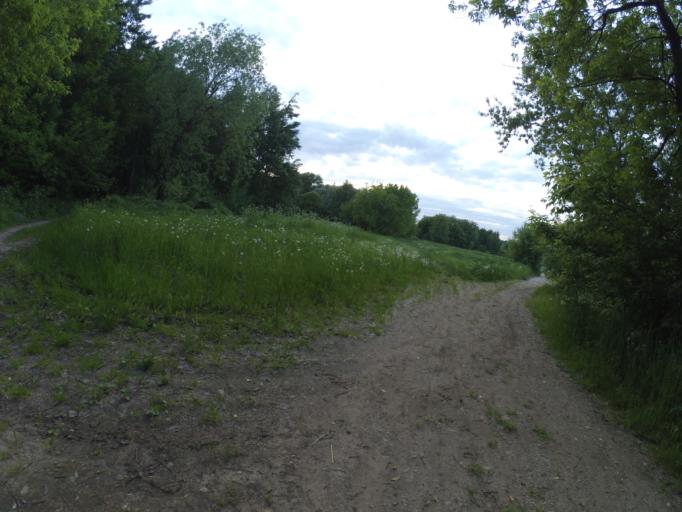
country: RU
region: Moscow
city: Kolomenskoye
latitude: 55.6474
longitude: 37.6794
